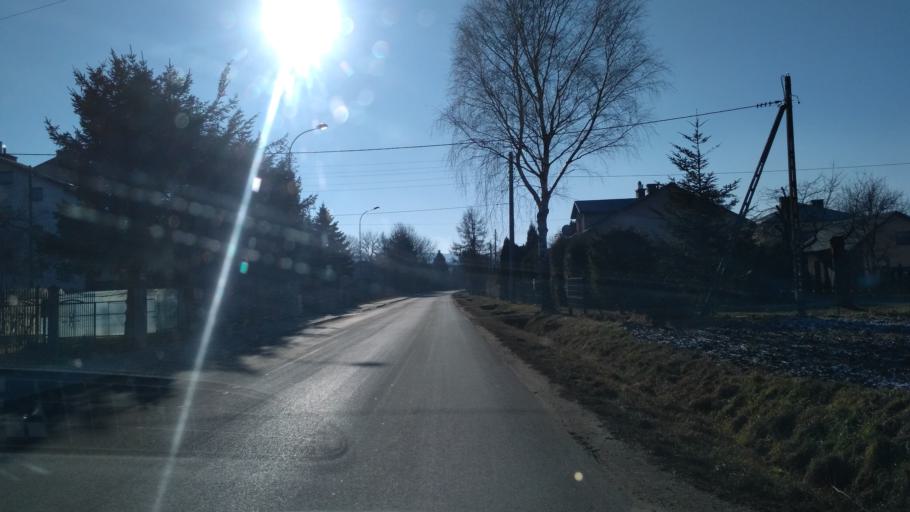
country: PL
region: Subcarpathian Voivodeship
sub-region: Powiat krosnienski
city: Rymanow
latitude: 49.5850
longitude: 21.8664
